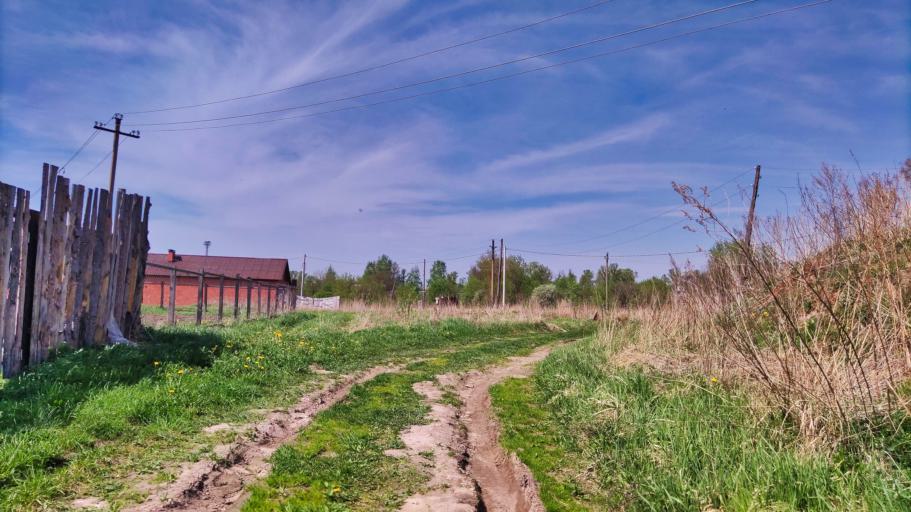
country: RU
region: Tverskaya
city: Rzhev
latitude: 56.2363
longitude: 34.3261
